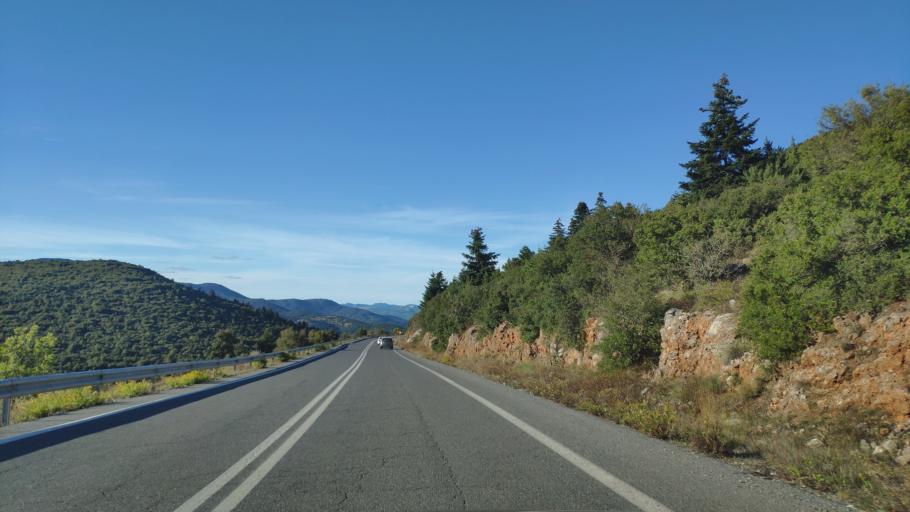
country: GR
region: Peloponnese
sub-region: Nomos Arkadias
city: Langadhia
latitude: 37.6988
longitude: 22.1989
